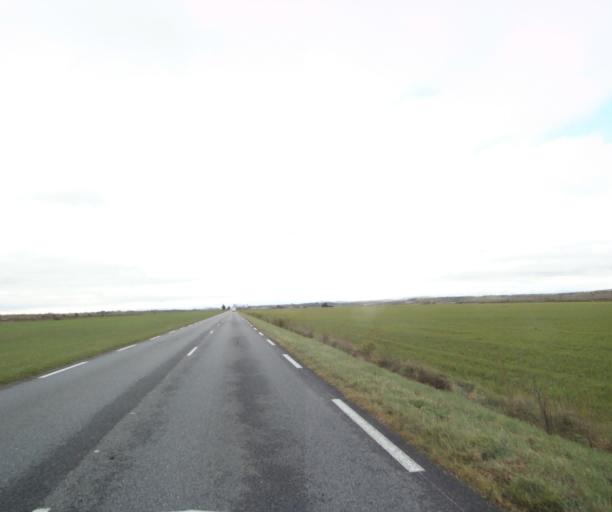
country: FR
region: Midi-Pyrenees
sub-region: Departement de l'Ariege
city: Saverdun
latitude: 43.2703
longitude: 1.5517
